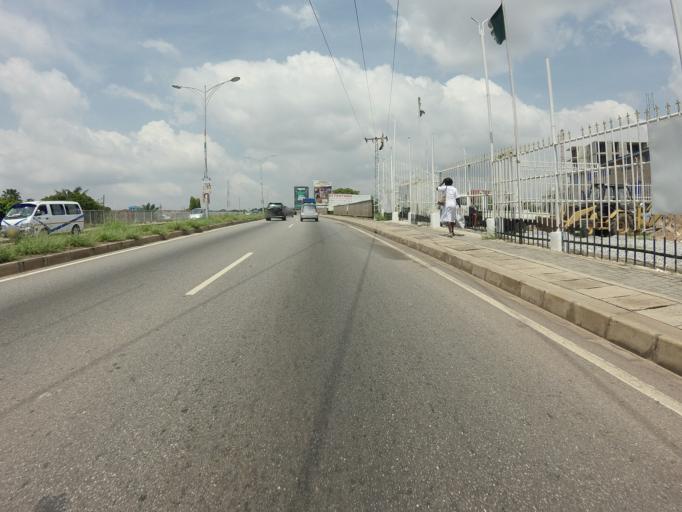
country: GH
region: Greater Accra
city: Dome
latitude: 5.6125
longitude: -0.2127
